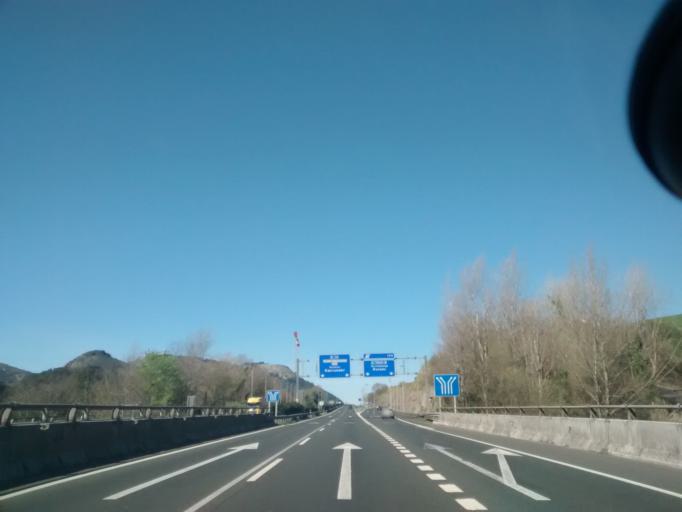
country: ES
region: Cantabria
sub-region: Provincia de Cantabria
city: Lierganes
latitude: 43.3886
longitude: -3.7335
